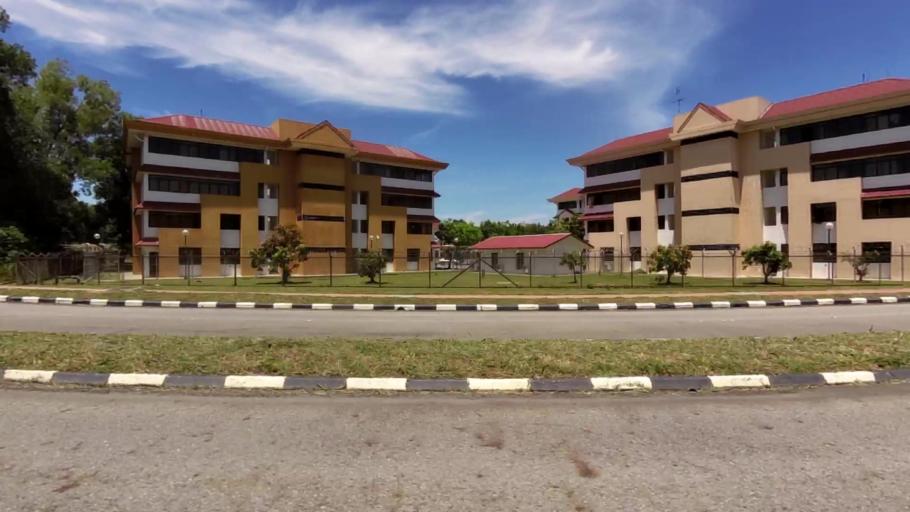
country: BN
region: Brunei and Muara
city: Bandar Seri Begawan
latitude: 4.9310
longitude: 114.9514
